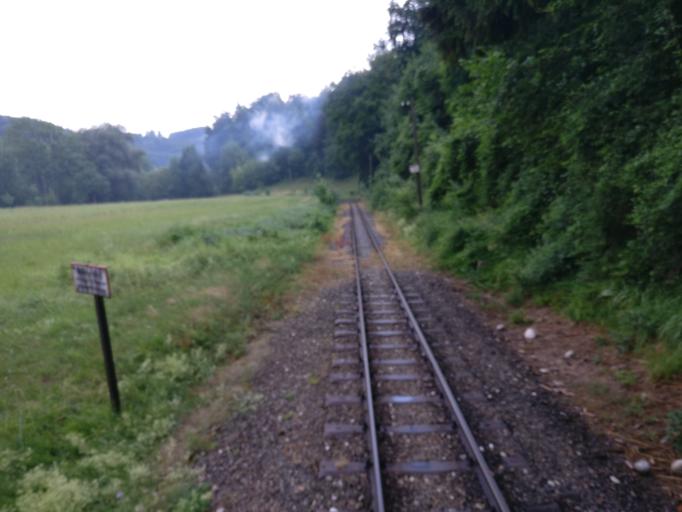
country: AT
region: Upper Austria
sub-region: Politischer Bezirk Steyr-Land
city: Waldneukirchen
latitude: 47.9908
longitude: 14.2805
